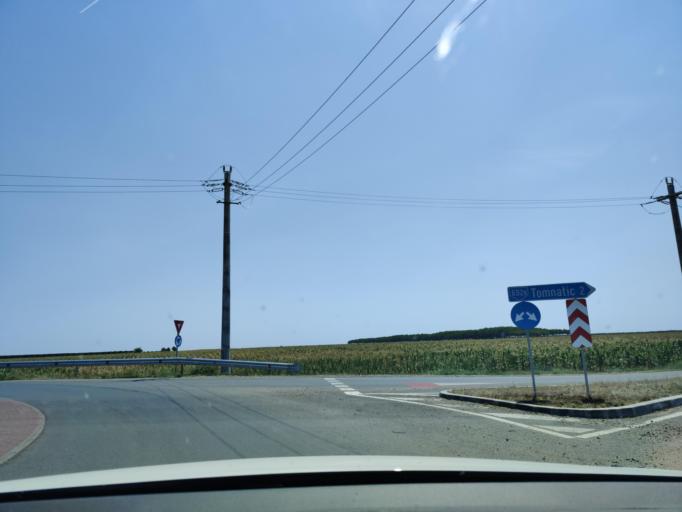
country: RO
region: Timis
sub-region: Comuna Tomnatic
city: Tomnatic
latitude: 45.9932
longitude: 20.6890
